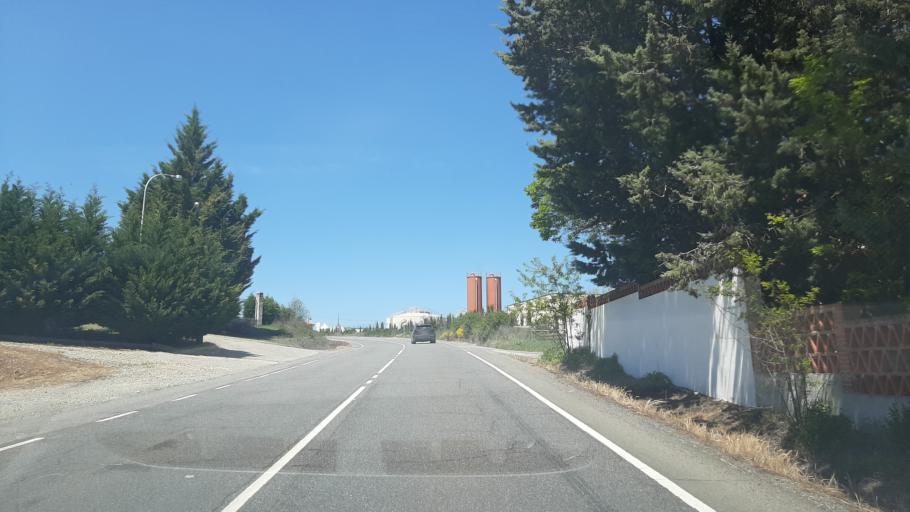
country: ES
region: Castille and Leon
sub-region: Provincia de Salamanca
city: Guijo de Avila
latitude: 40.5551
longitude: -5.6402
